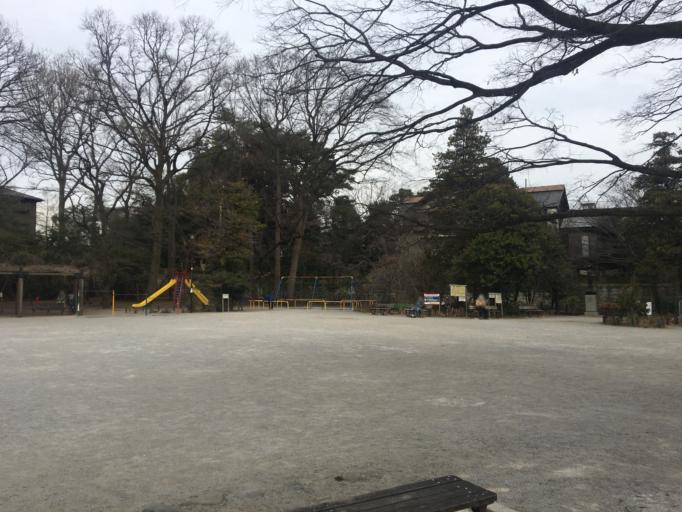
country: JP
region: Tokyo
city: Musashino
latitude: 35.7272
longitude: 139.5674
